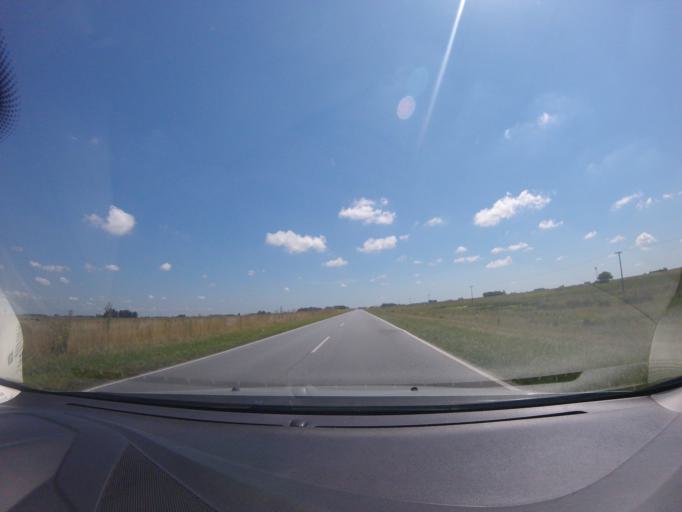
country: AR
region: Buenos Aires
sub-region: Partido de Rauch
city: Rauch
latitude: -36.8749
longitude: -58.9897
